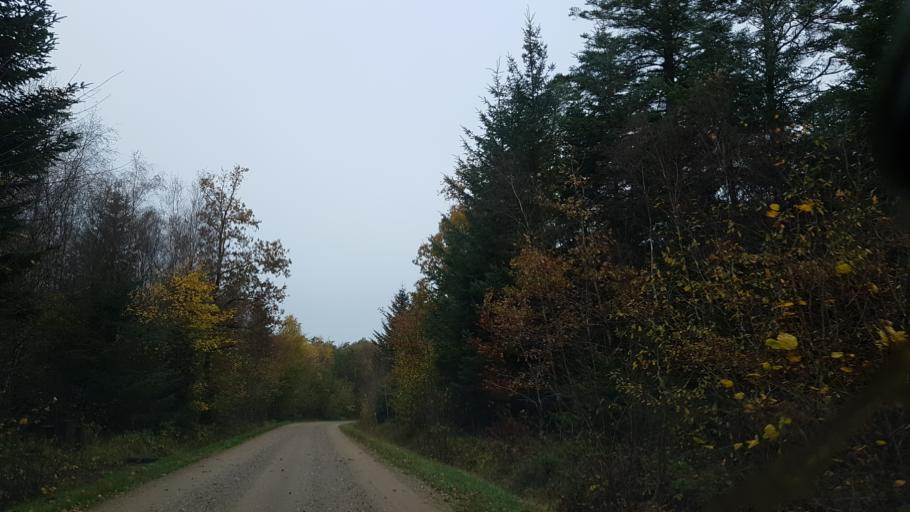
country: DK
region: South Denmark
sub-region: Tonder Kommune
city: Sherrebek
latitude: 55.1899
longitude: 8.7573
